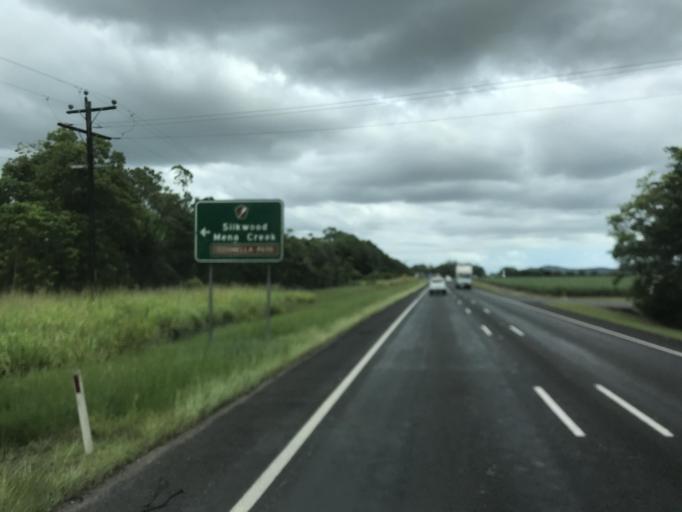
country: AU
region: Queensland
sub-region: Cassowary Coast
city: Innisfail
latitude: -17.7532
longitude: 146.0277
